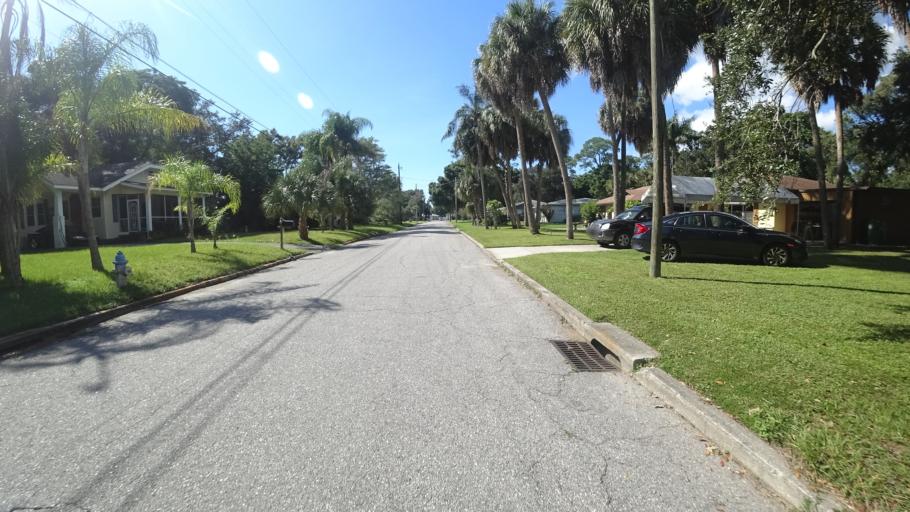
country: US
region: Florida
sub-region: Manatee County
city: Bradenton
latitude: 27.4837
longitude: -82.5814
